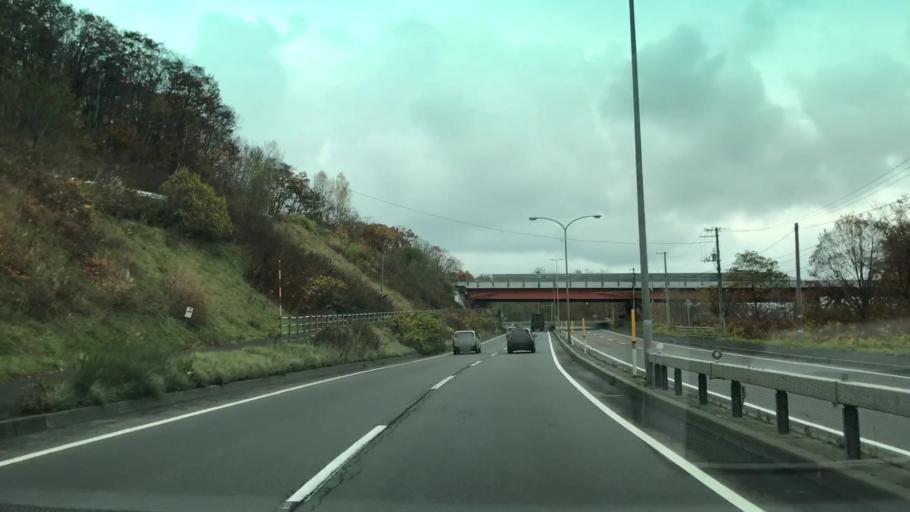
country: JP
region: Hokkaido
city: Otaru
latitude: 43.1550
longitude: 141.1102
